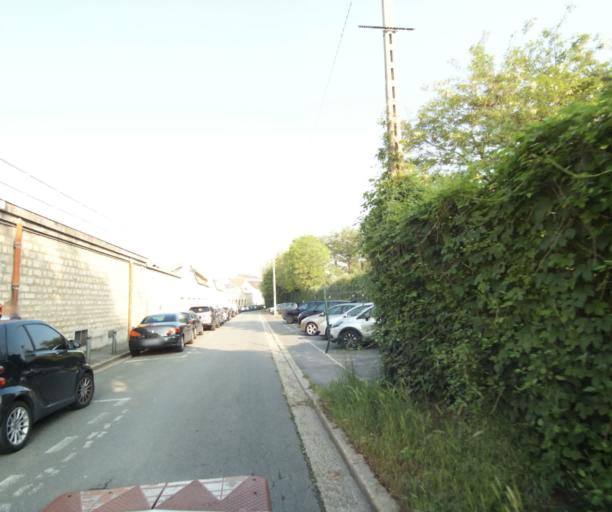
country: FR
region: Ile-de-France
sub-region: Departement du Val-d'Oise
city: Argenteuil
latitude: 48.9476
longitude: 2.2605
